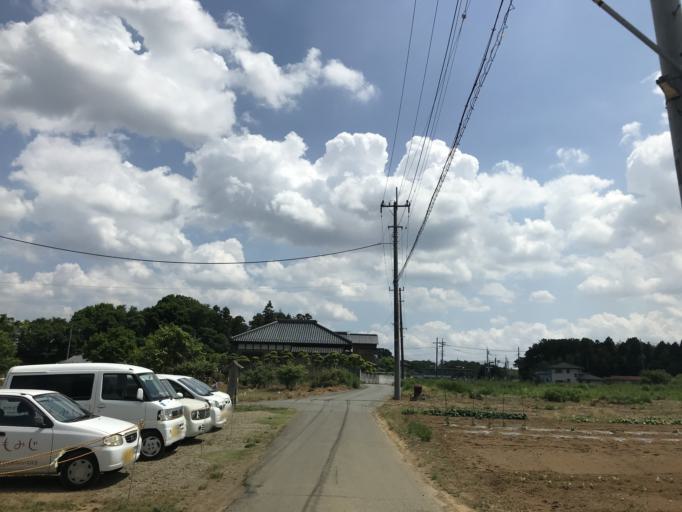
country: JP
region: Ibaraki
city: Mitsukaido
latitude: 36.0697
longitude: 140.0434
